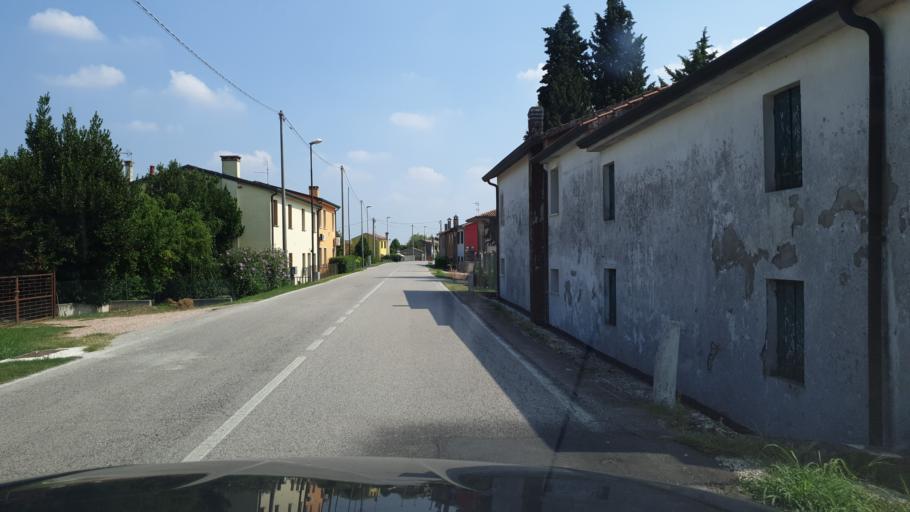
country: IT
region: Veneto
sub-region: Provincia di Rovigo
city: Villamarzana
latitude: 45.0122
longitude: 11.7040
